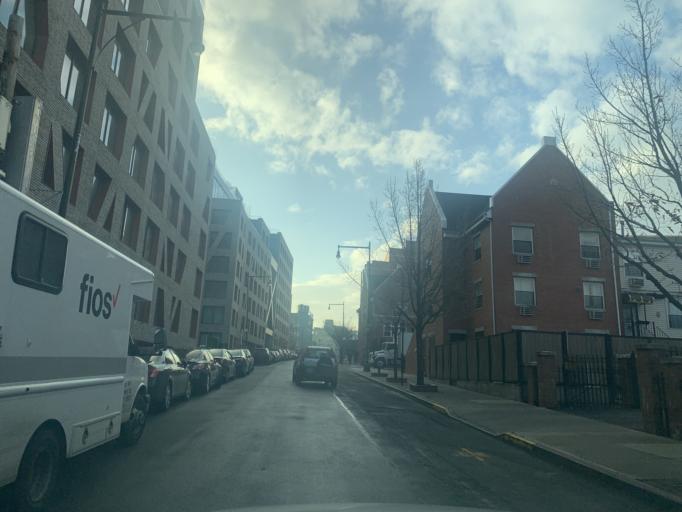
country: US
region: New York
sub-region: Queens County
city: Long Island City
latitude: 40.7003
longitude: -73.9345
